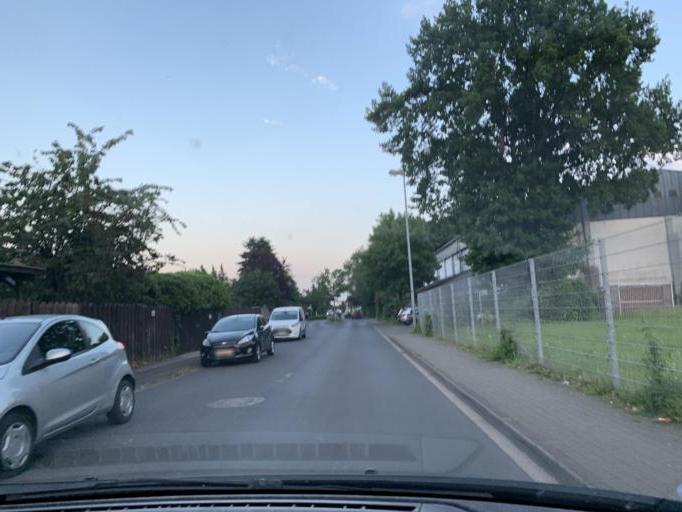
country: DE
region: North Rhine-Westphalia
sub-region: Regierungsbezirk Koln
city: Pulheim
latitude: 51.0025
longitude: 6.8129
